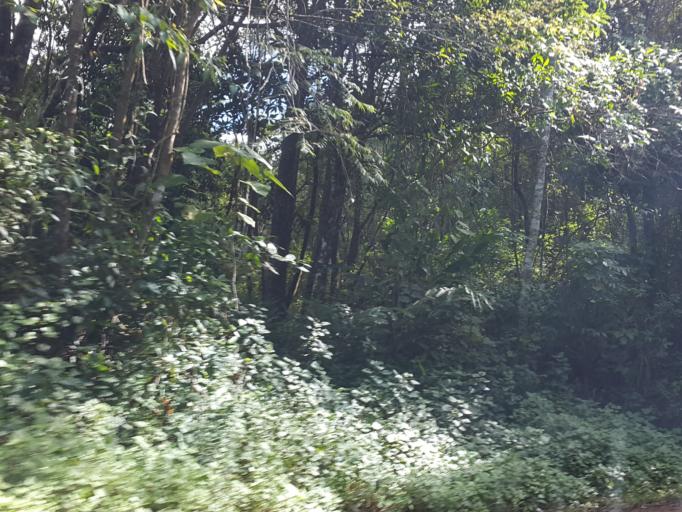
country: TH
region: Chiang Mai
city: Wiang Haeng
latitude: 19.5543
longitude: 98.8096
